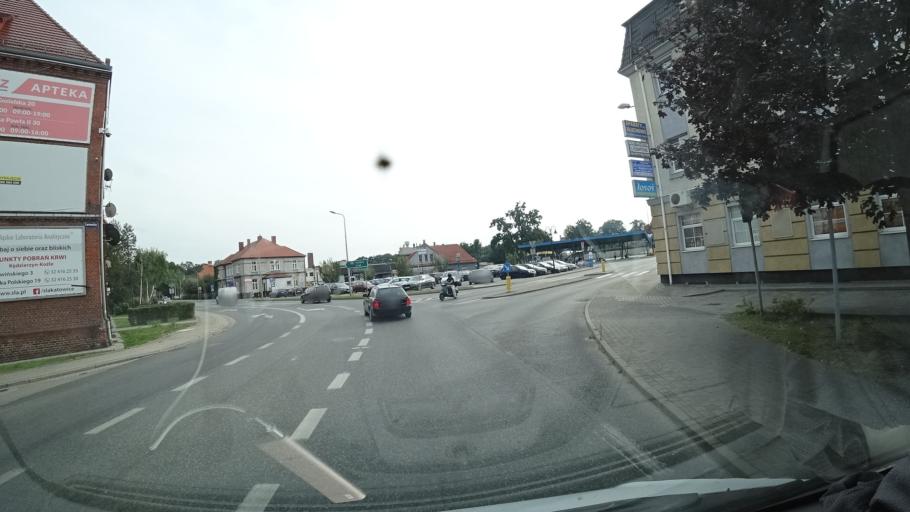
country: PL
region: Opole Voivodeship
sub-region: Powiat kedzierzynsko-kozielski
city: Kozle
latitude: 50.3333
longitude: 18.1486
